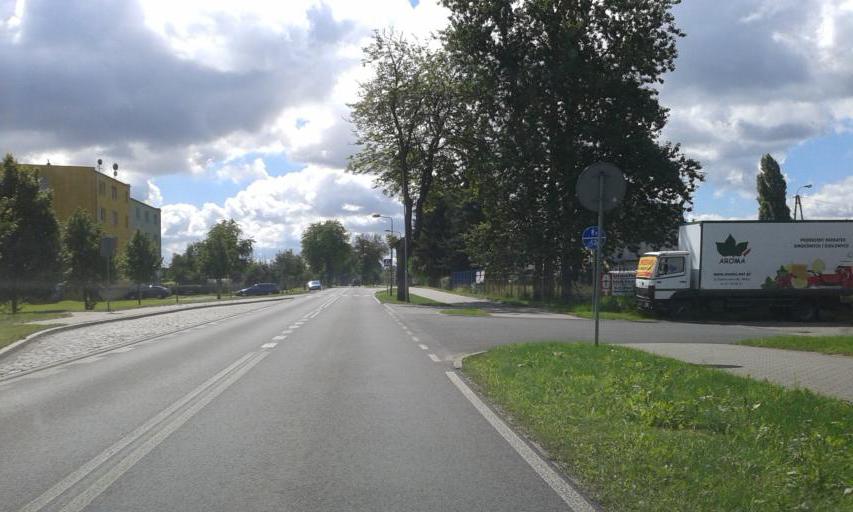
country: PL
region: West Pomeranian Voivodeship
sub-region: Powiat walecki
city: Walcz
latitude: 53.2883
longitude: 16.4596
